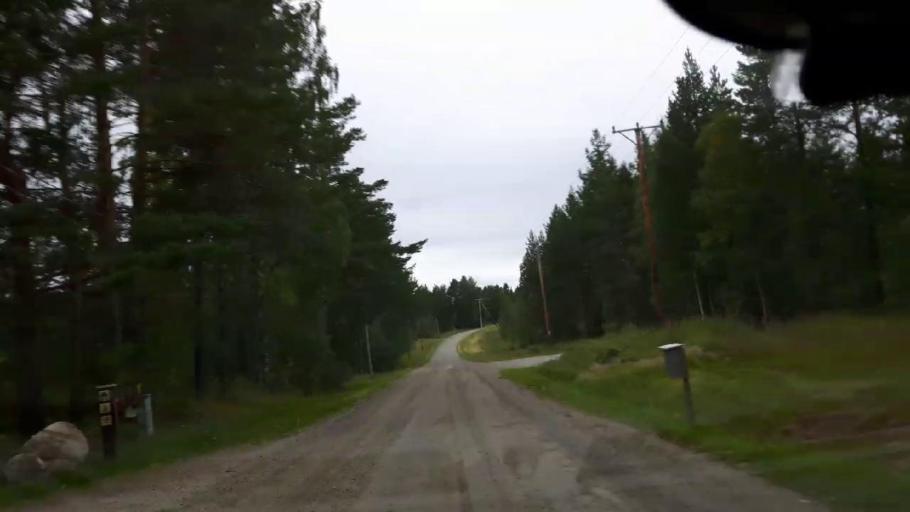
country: SE
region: Vaesternorrland
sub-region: Ange Kommun
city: Fransta
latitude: 62.7957
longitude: 16.0299
